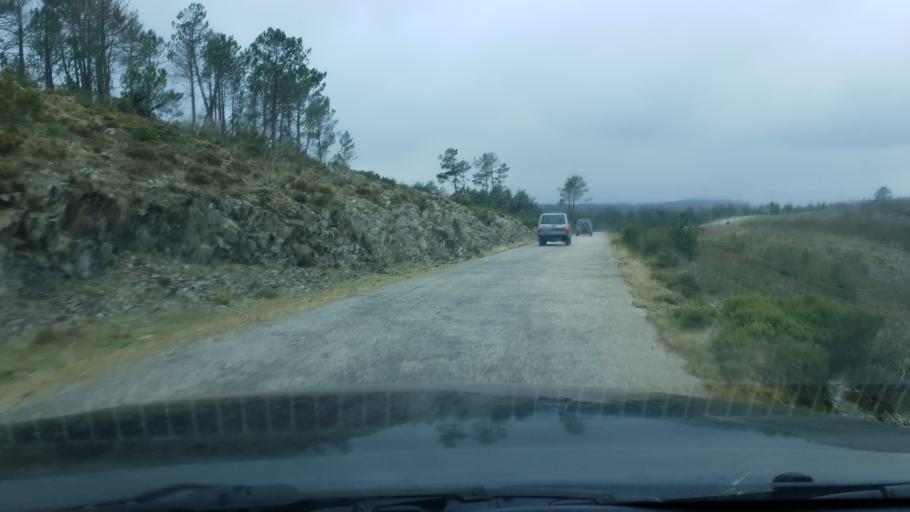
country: PT
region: Viseu
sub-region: Sao Pedro do Sul
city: Sao Pedro do Sul
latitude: 40.8689
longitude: -8.0818
